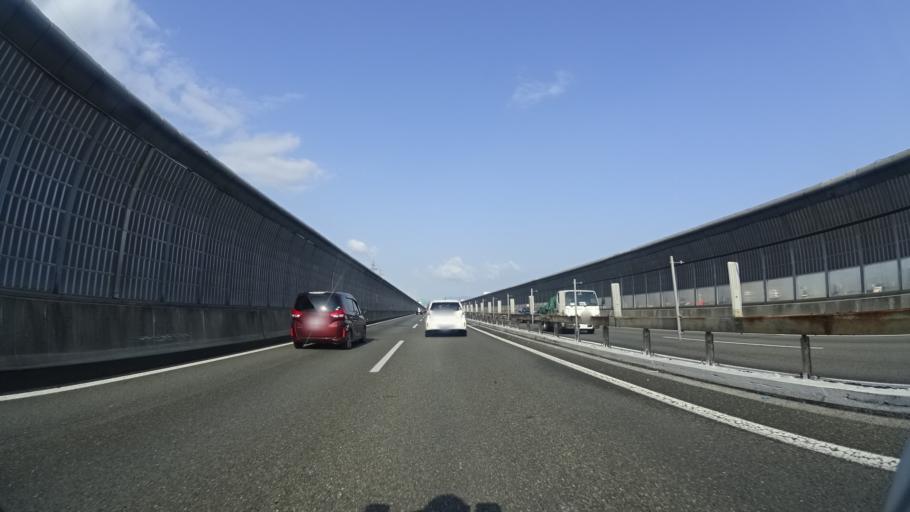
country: JP
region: Hyogo
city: Amagasaki
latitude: 34.7436
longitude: 135.4309
